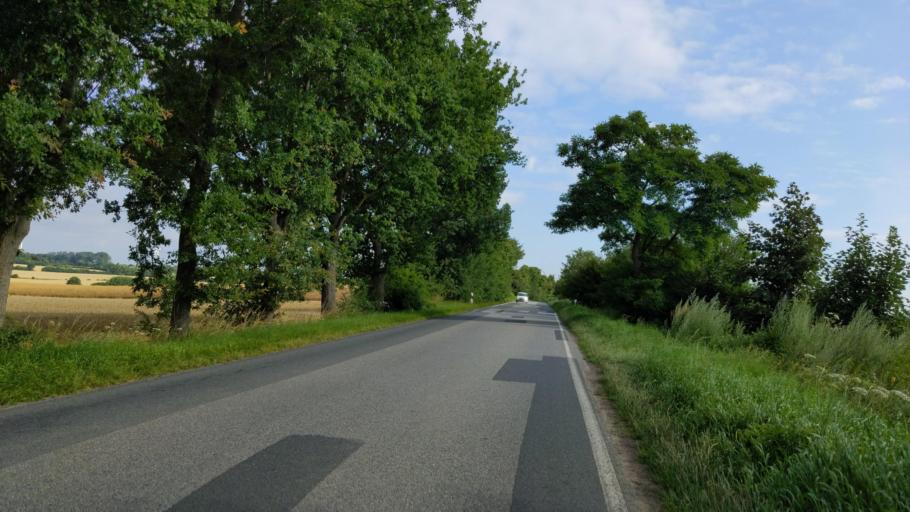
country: DE
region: Schleswig-Holstein
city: Bad Schwartau
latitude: 53.9854
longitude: 10.6606
